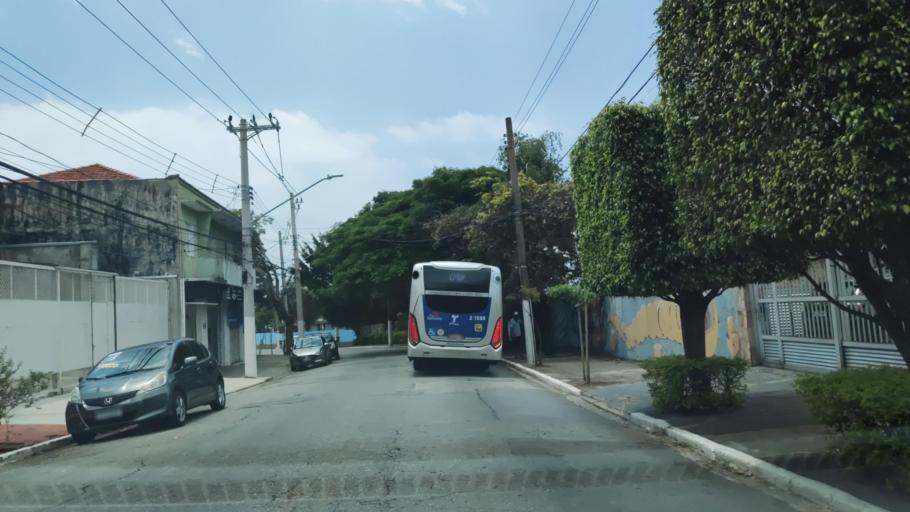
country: BR
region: Sao Paulo
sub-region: Sao Paulo
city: Sao Paulo
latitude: -23.5011
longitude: -46.6485
